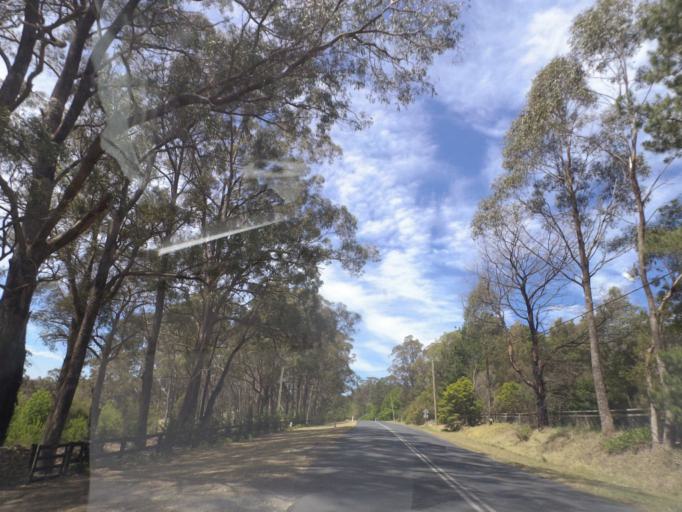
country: AU
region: New South Wales
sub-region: Wingecarribee
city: Colo Vale
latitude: -34.4102
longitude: 150.5208
